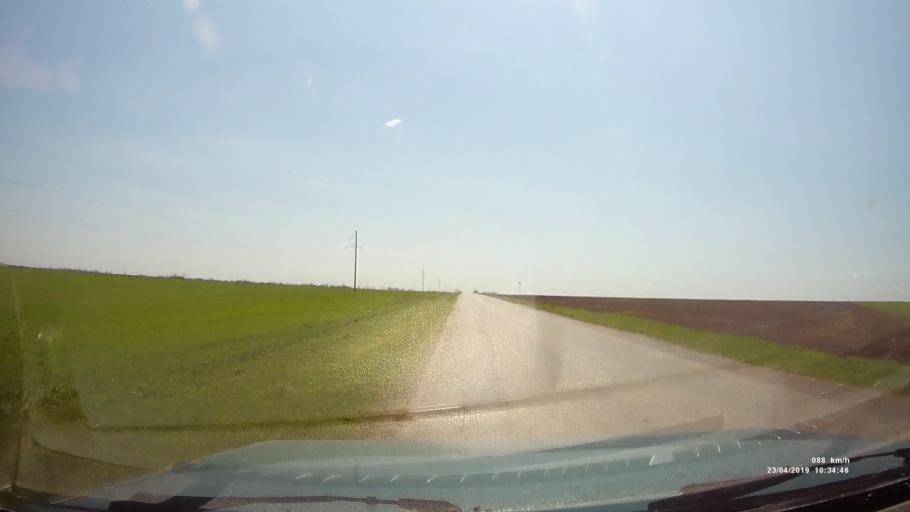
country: RU
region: Kalmykiya
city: Yashalta
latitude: 46.5607
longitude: 42.6149
